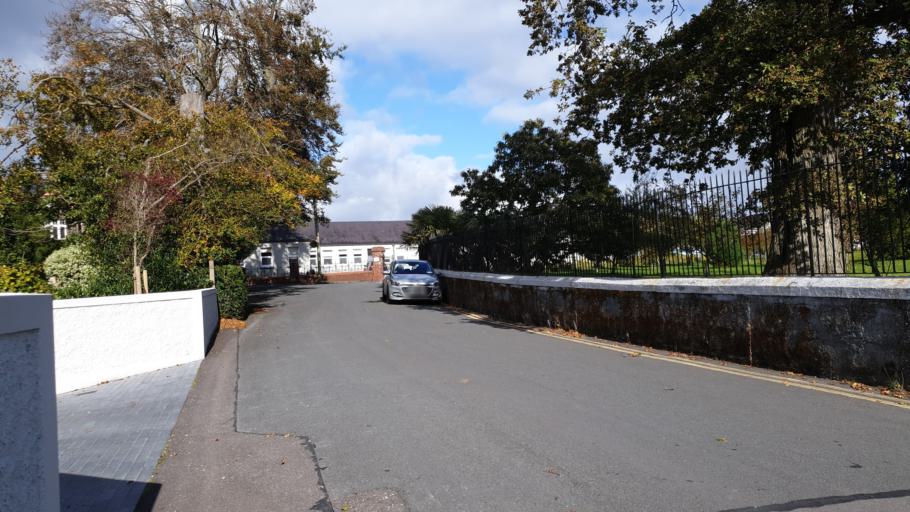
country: IE
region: Munster
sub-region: County Cork
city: Cork
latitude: 51.8974
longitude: -8.4313
